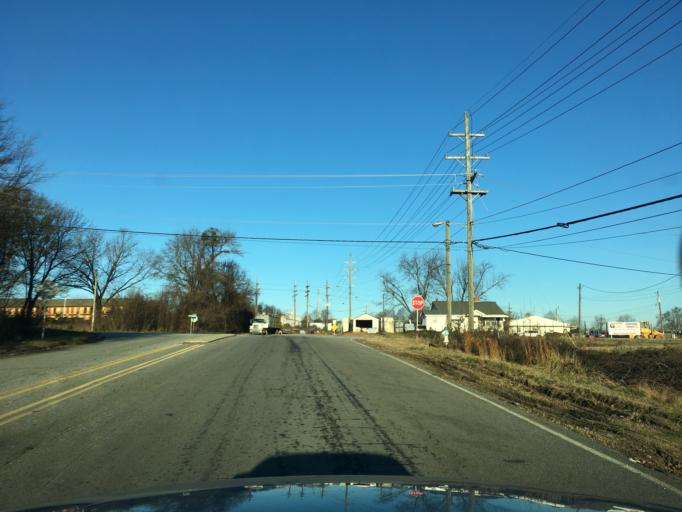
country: US
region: South Carolina
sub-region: Spartanburg County
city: Wellford
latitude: 34.9172
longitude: -82.1079
